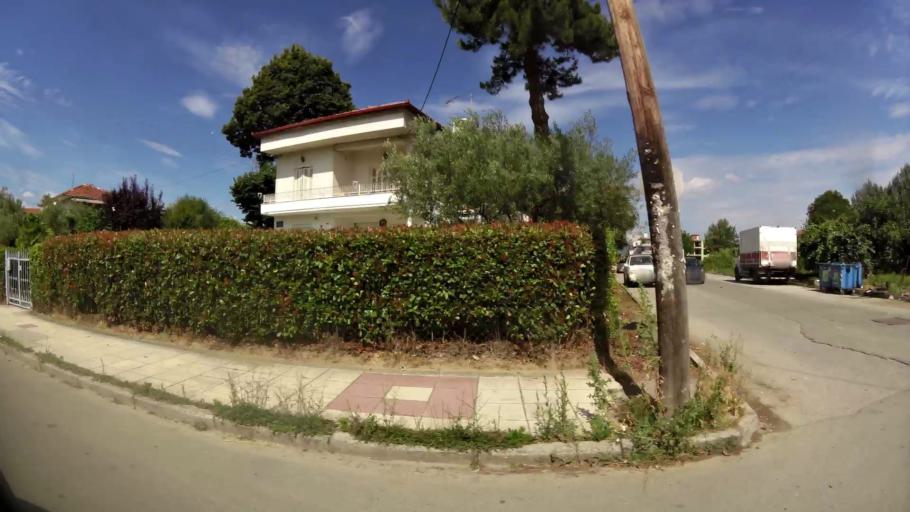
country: GR
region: Central Macedonia
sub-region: Nomos Pierias
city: Katerini
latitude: 40.2746
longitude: 22.4917
